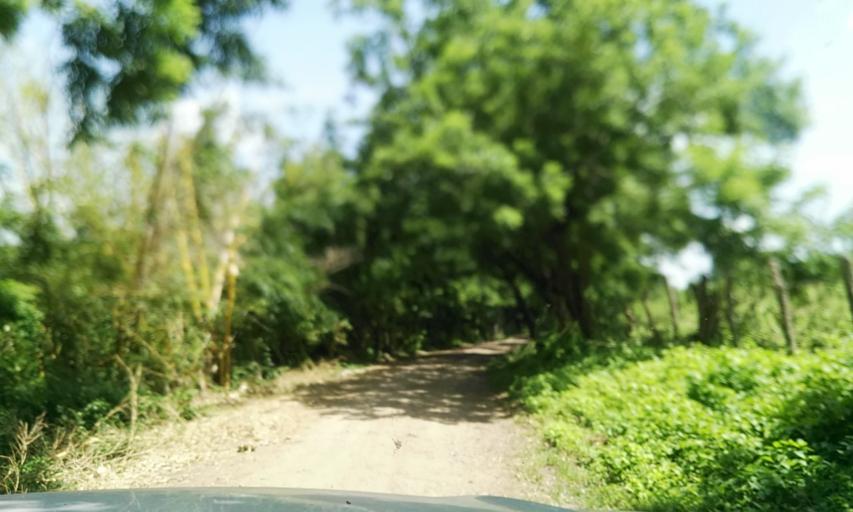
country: NI
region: Matagalpa
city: Terrabona
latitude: 12.7181
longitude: -85.9240
